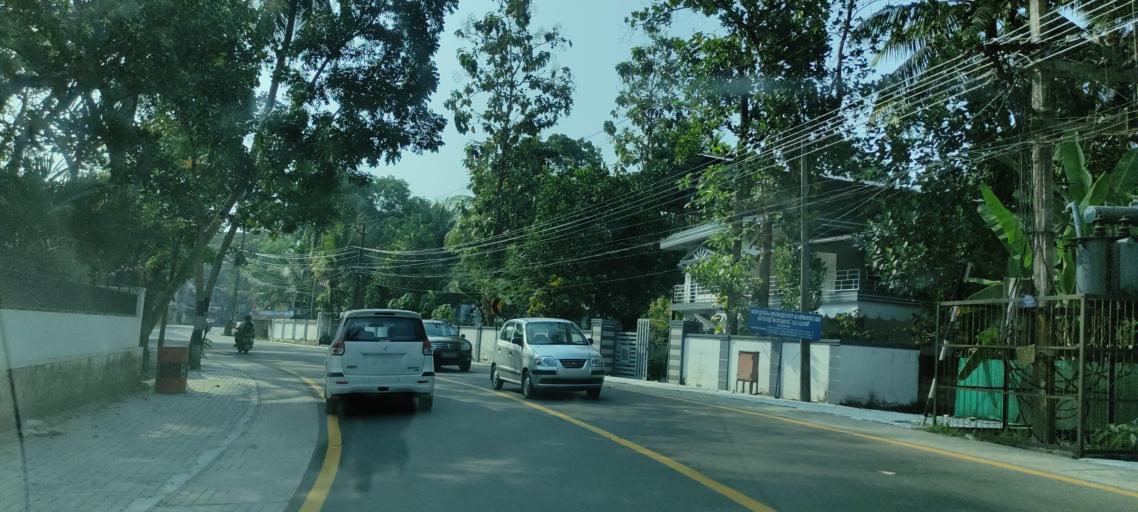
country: IN
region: Kerala
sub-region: Pattanamtitta
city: Tiruvalla
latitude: 9.3705
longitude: 76.5250
